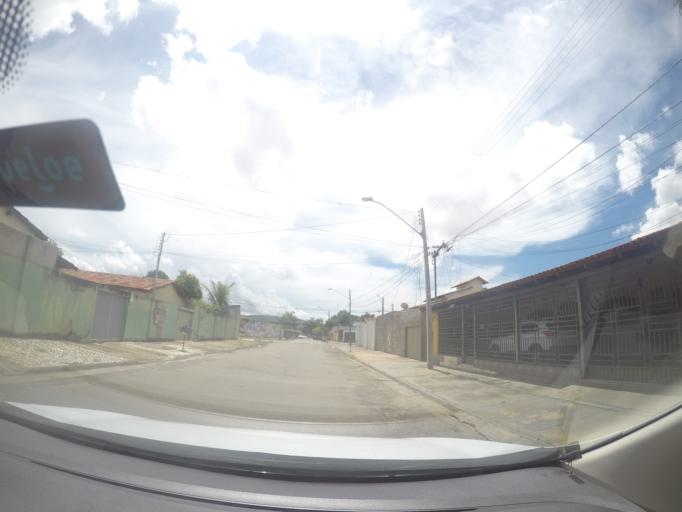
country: BR
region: Goias
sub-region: Goiania
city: Goiania
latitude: -16.6780
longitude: -49.3134
